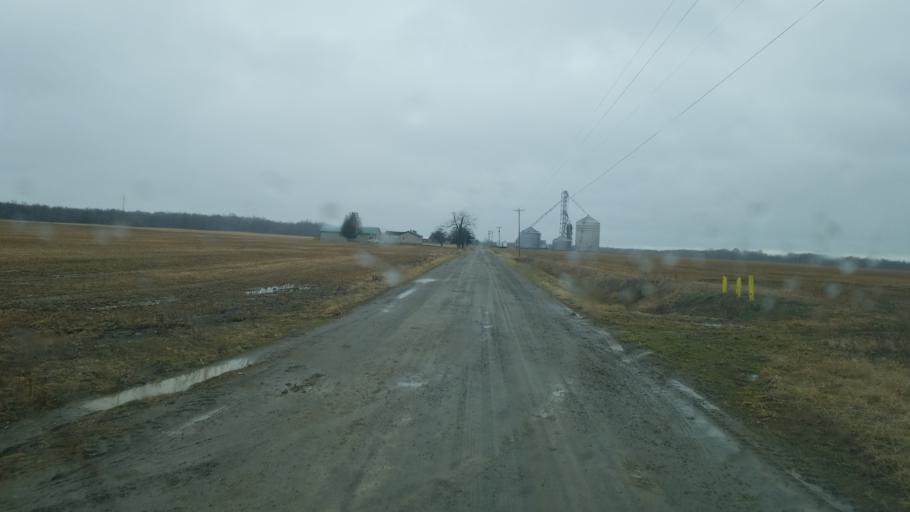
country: US
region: Ohio
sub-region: Ashtabula County
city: Roaming Shores
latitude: 41.5868
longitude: -80.7194
